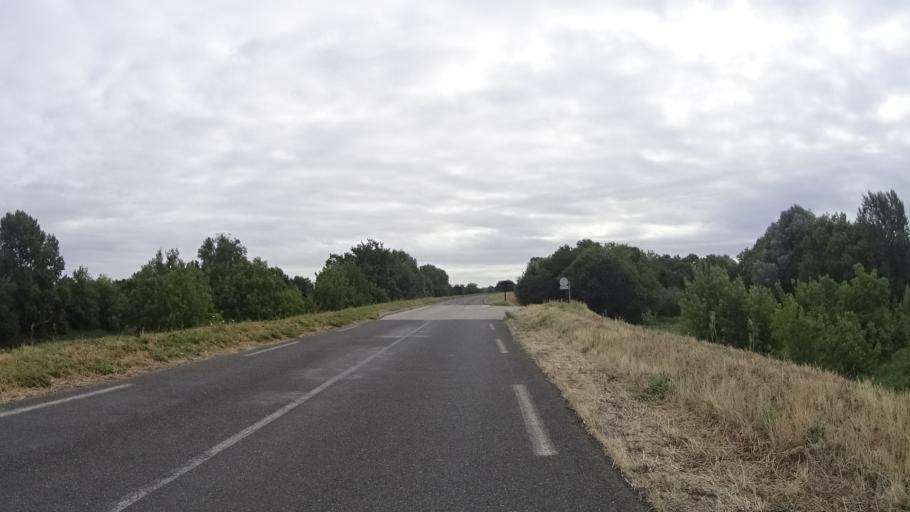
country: FR
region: Pays de la Loire
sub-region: Departement de Maine-et-Loire
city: Saint-Florent-le-Vieil
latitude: 47.3643
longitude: -1.0010
